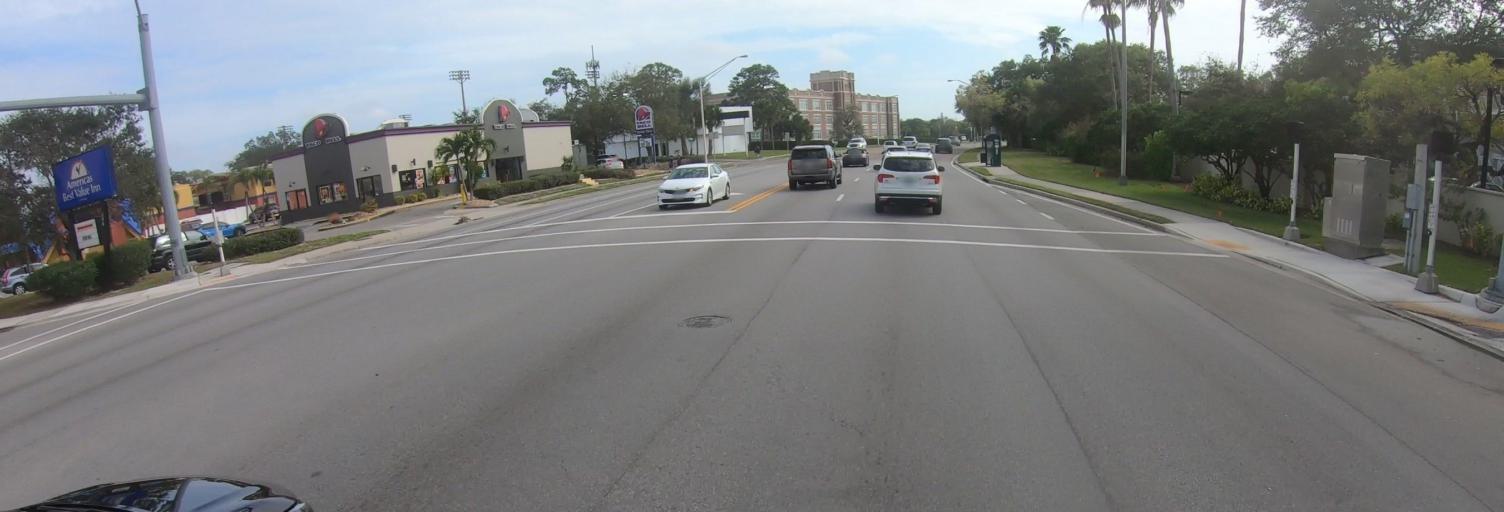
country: US
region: Florida
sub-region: Sarasota County
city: Sarasota
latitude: 27.3276
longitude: -82.5304
